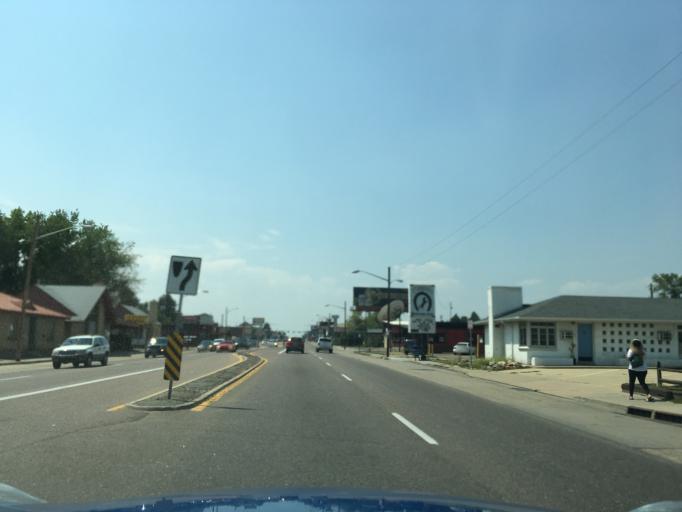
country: US
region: Colorado
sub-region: Adams County
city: Aurora
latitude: 39.7402
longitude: -104.8880
